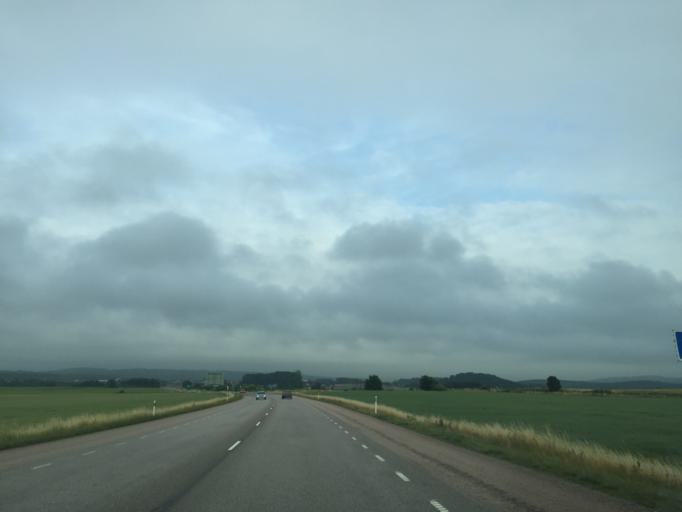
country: SE
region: Halland
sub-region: Falkenbergs Kommun
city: Falkenberg
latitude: 56.8828
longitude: 12.5791
